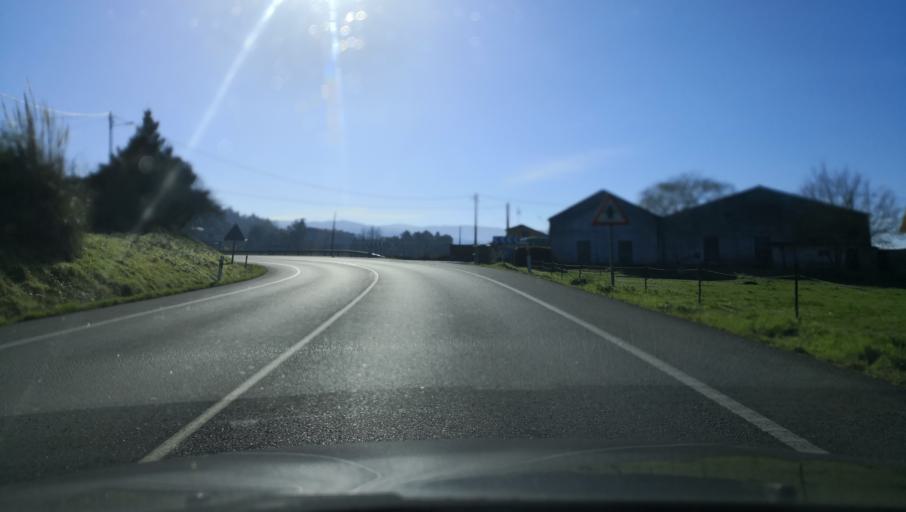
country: ES
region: Galicia
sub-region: Provincia da Coruna
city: Ribeira
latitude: 42.7596
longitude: -8.3986
